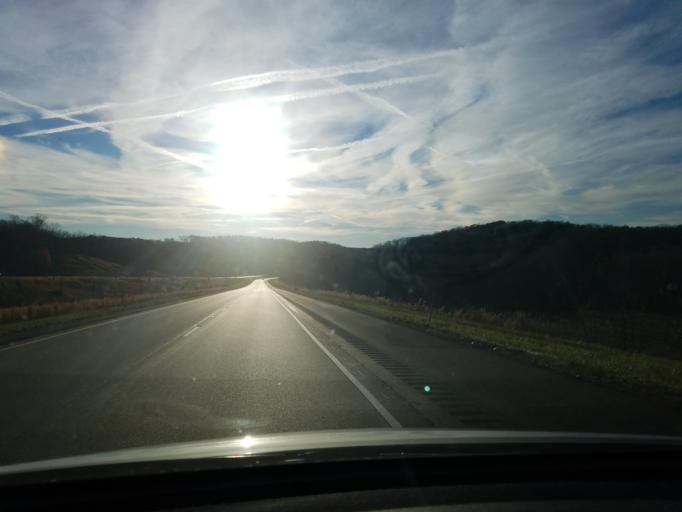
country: US
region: Indiana
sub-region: Crawford County
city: English
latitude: 38.2307
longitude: -86.6307
